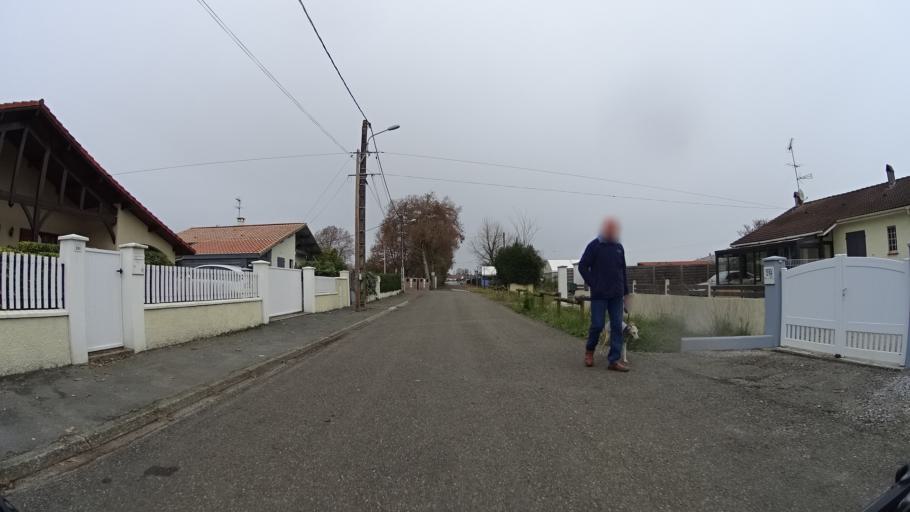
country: FR
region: Aquitaine
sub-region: Departement des Landes
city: Saint-Paul-les-Dax
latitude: 43.7330
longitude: -1.0514
